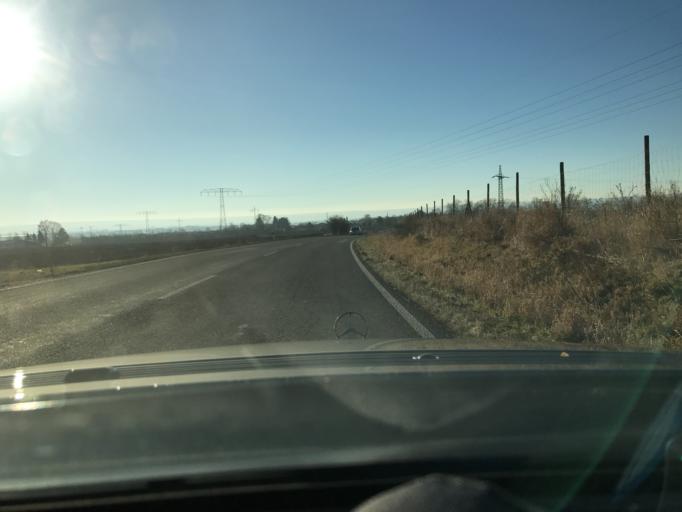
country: DE
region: Thuringia
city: Muehlhausen
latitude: 51.2347
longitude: 10.4835
